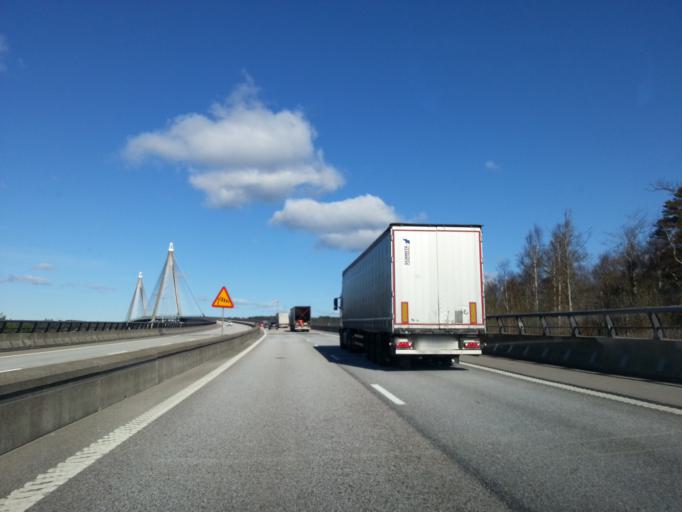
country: SE
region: Vaestra Goetaland
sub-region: Uddevalla Kommun
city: Uddevalla
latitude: 58.3189
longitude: 11.8553
